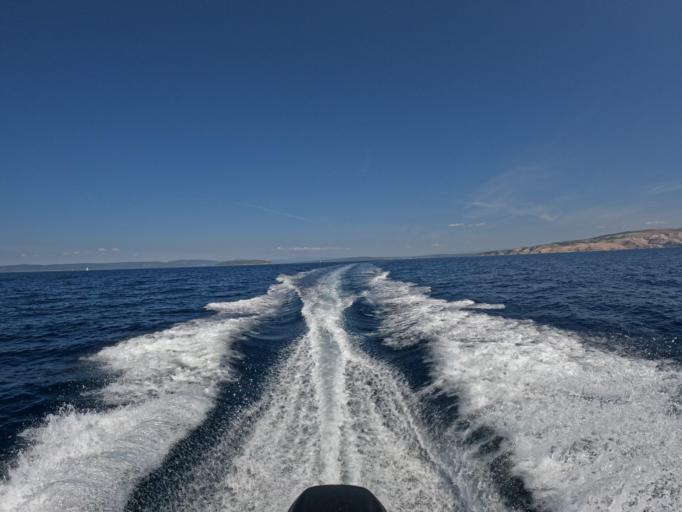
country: HR
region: Primorsko-Goranska
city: Punat
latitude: 44.9078
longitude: 14.6297
